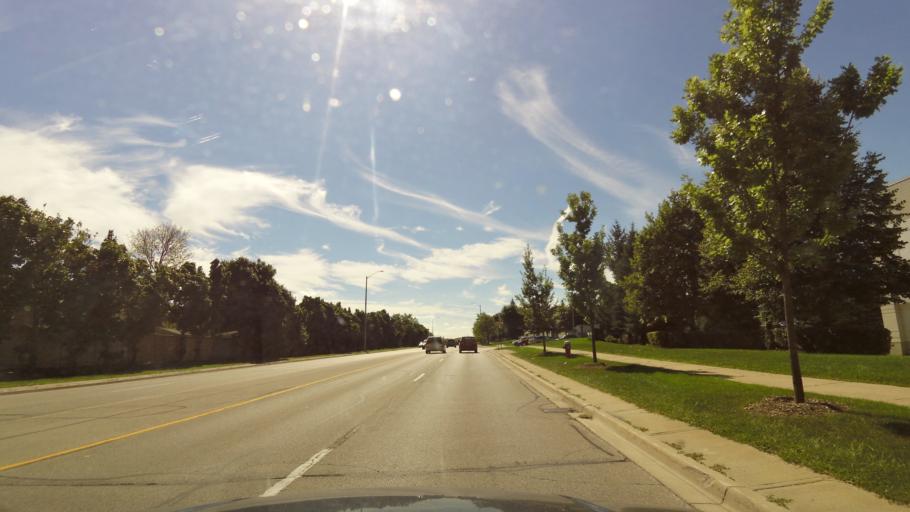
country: CA
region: Ontario
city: Mississauga
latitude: 43.6111
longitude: -79.6871
